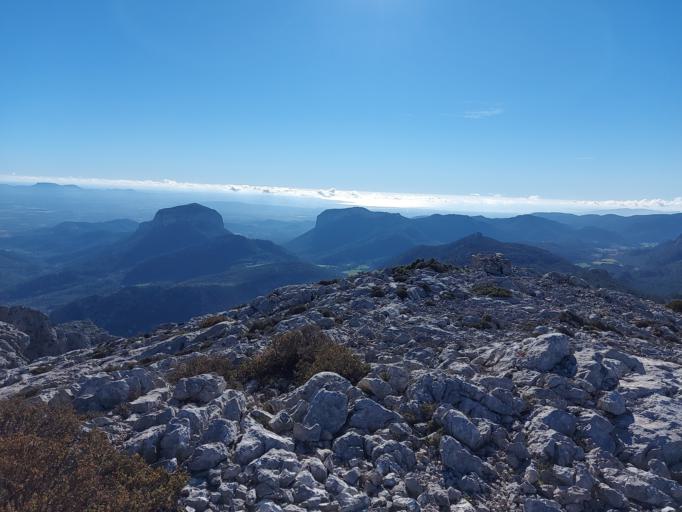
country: ES
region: Balearic Islands
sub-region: Illes Balears
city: Fornalutx
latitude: 39.7821
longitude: 2.8079
